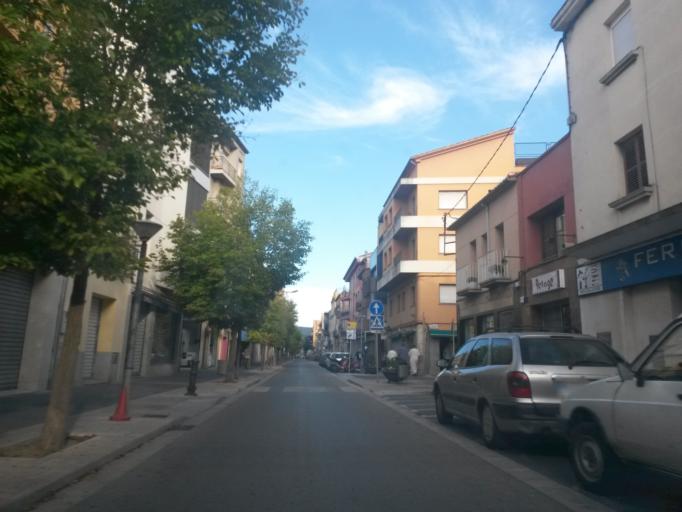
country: ES
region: Catalonia
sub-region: Provincia de Girona
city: Salt
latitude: 41.9760
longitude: 2.7972
